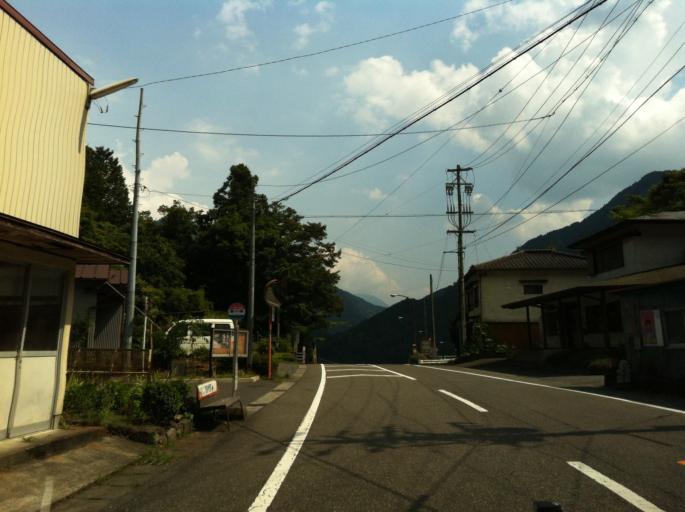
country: JP
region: Shizuoka
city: Shizuoka-shi
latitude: 35.2378
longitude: 138.3417
